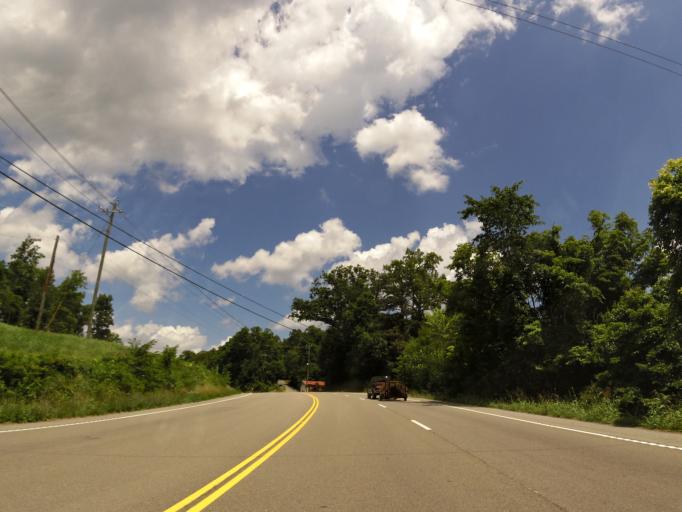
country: US
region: Tennessee
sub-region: Union County
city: Maynardville
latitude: 36.2729
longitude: -83.7664
